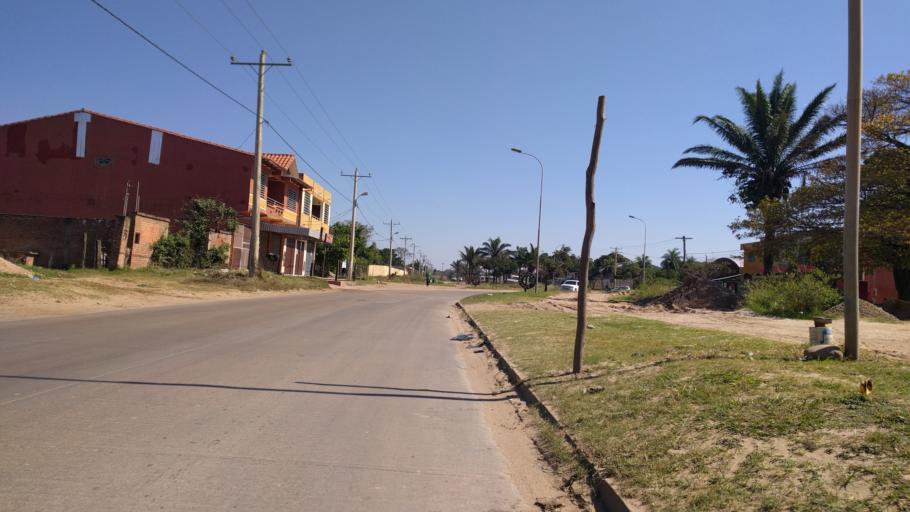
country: BO
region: Santa Cruz
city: Santa Cruz de la Sierra
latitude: -17.8478
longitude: -63.2065
